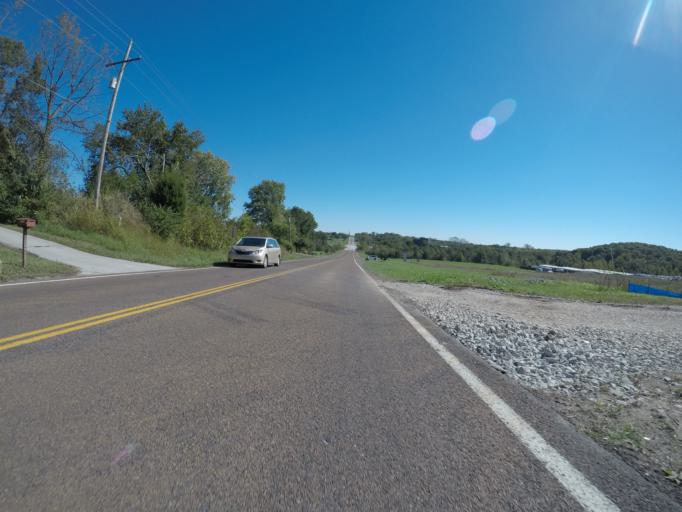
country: US
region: Kansas
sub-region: Wyandotte County
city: Bonner Springs
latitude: 39.0580
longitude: -94.9064
